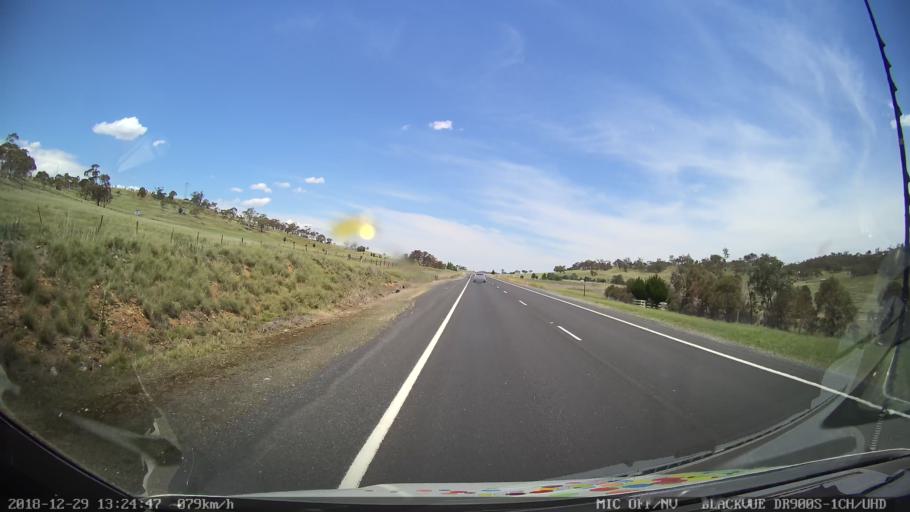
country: AU
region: New South Wales
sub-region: Cooma-Monaro
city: Cooma
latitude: -35.8341
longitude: 149.1622
